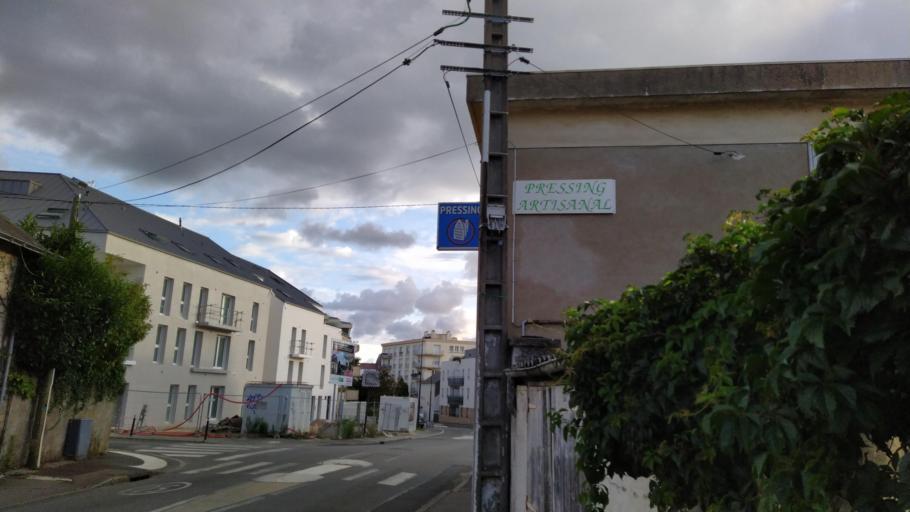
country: FR
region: Pays de la Loire
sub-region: Departement de la Loire-Atlantique
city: Nantes
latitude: 47.2366
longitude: -1.5402
